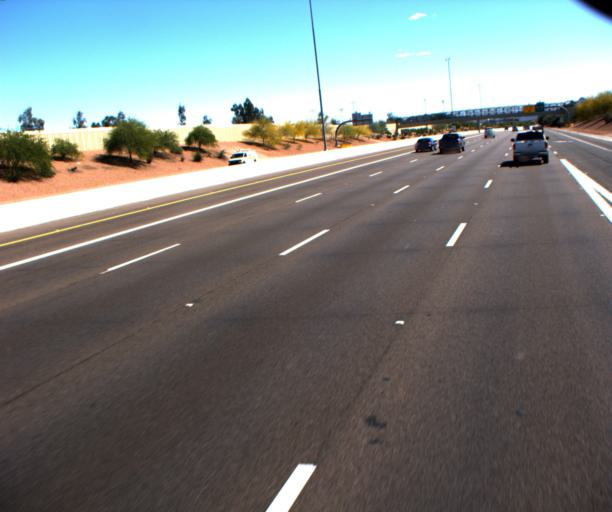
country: US
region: Arizona
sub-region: Maricopa County
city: Paradise Valley
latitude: 33.6510
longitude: -112.0007
